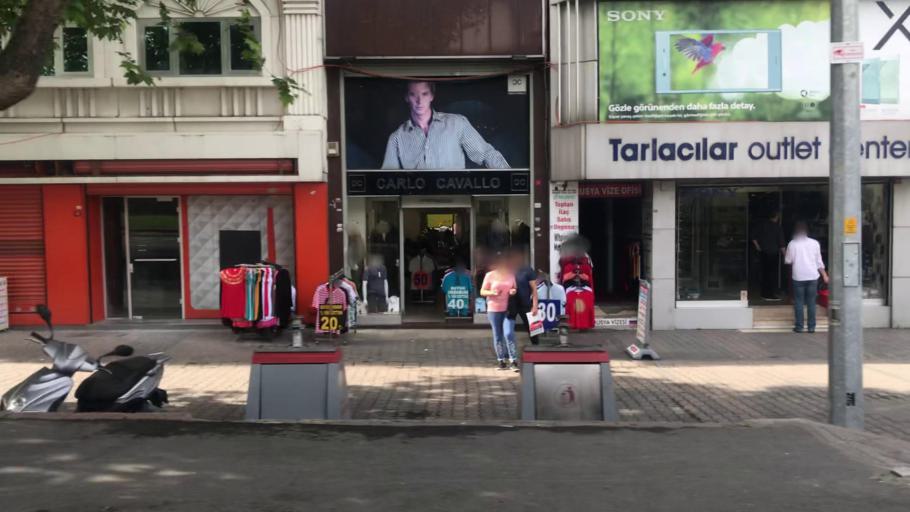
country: TR
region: Istanbul
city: Istanbul
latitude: 41.0094
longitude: 28.9510
